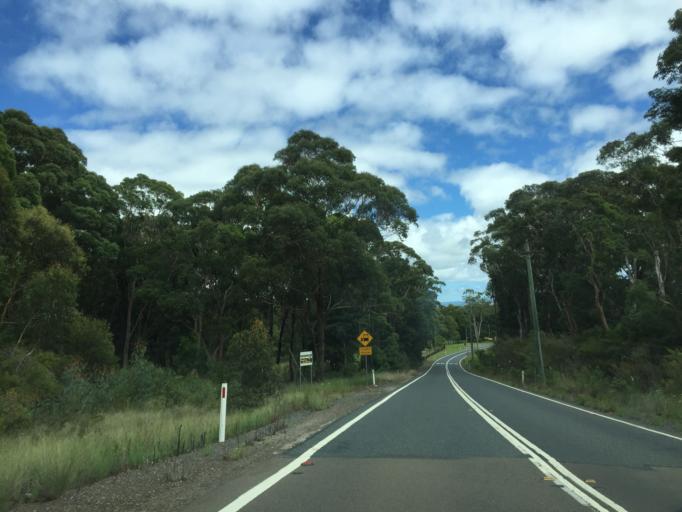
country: AU
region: New South Wales
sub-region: Hawkesbury
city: Richmond
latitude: -33.5196
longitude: 150.6189
